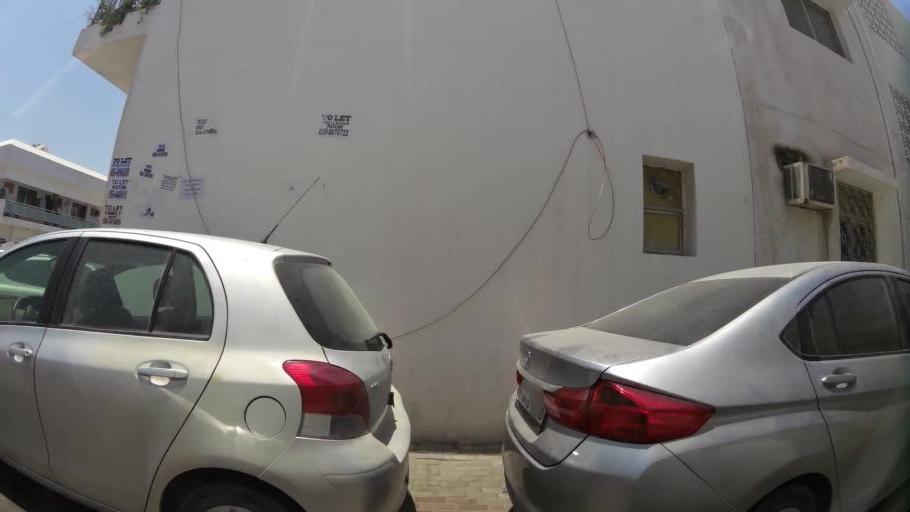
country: AE
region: Ash Shariqah
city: Sharjah
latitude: 25.2861
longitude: 55.3307
